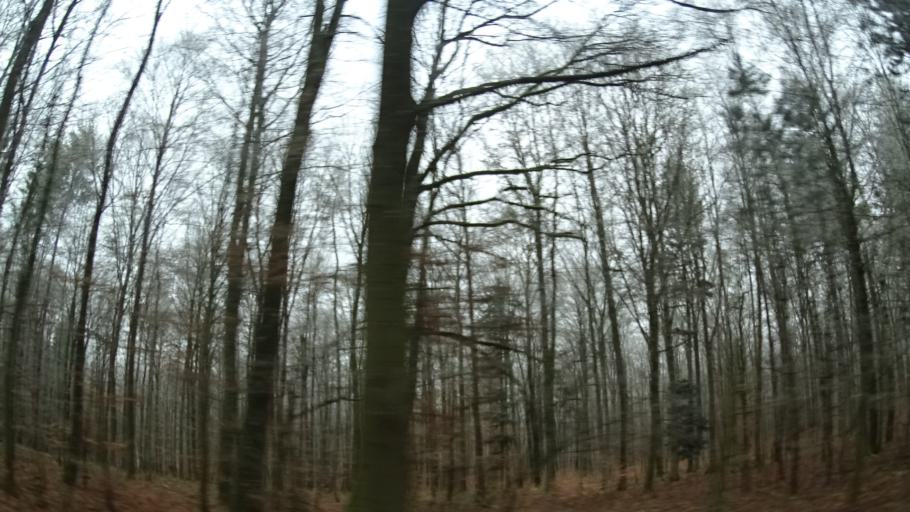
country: DE
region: Baden-Wuerttemberg
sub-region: Karlsruhe Region
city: Rosenberg
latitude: 49.4210
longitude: 9.5318
